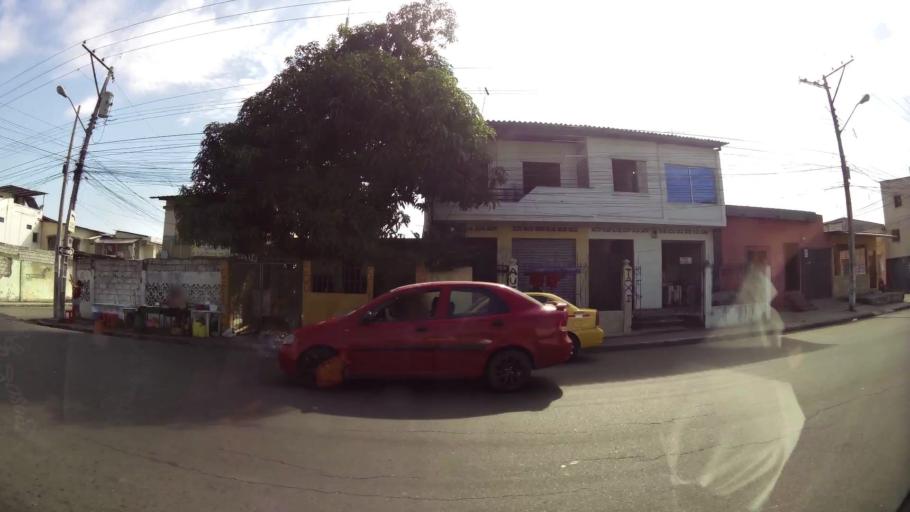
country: EC
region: Guayas
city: Guayaquil
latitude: -2.2053
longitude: -79.9115
